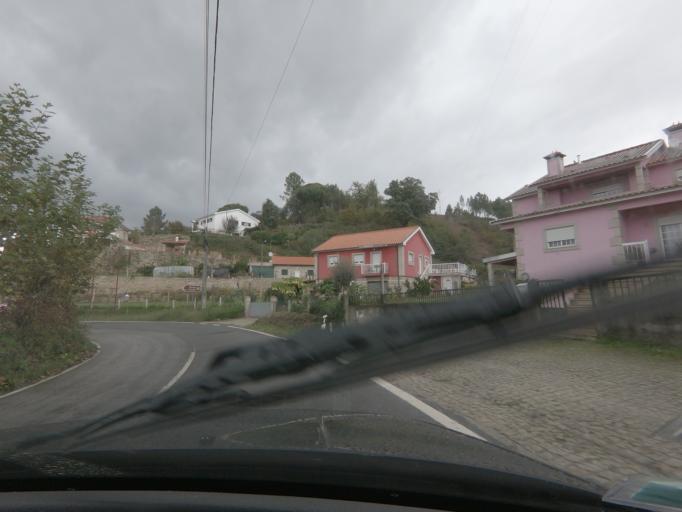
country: PT
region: Vila Real
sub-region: Mondim de Basto
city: Mondim de Basto
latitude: 41.4152
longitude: -7.9761
